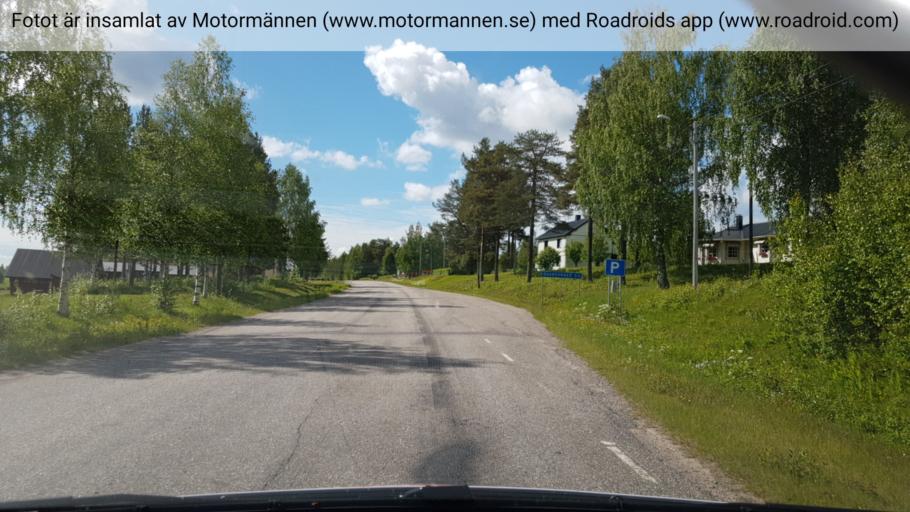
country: FI
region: Lapland
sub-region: Torniolaakso
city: Pello
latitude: 66.8011
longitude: 23.8969
